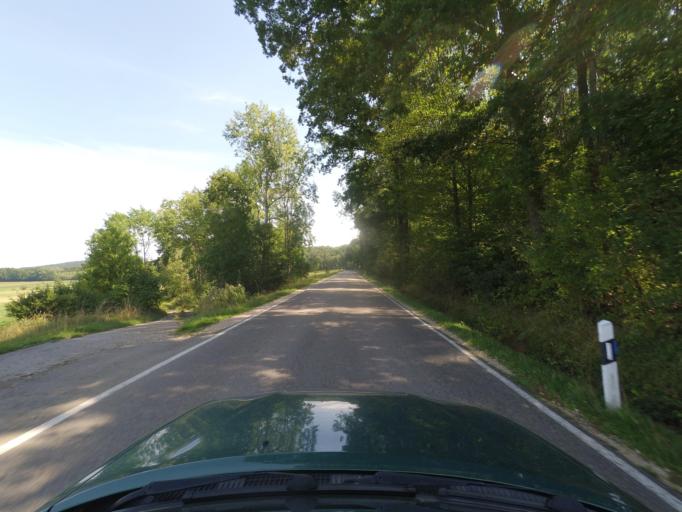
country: DE
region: Bavaria
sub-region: Regierungsbezirk Mittelfranken
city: Ettenstatt
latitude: 49.0750
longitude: 11.0739
